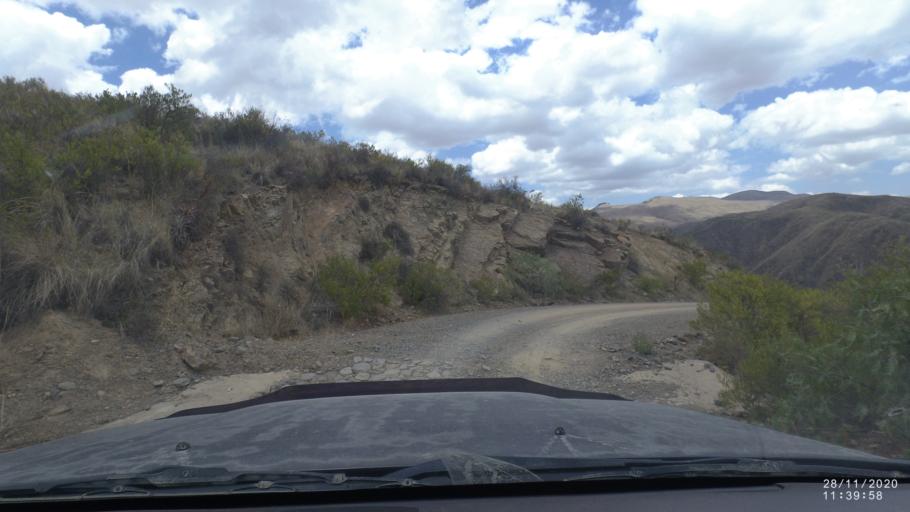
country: BO
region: Cochabamba
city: Tarata
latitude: -17.6748
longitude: -66.0448
